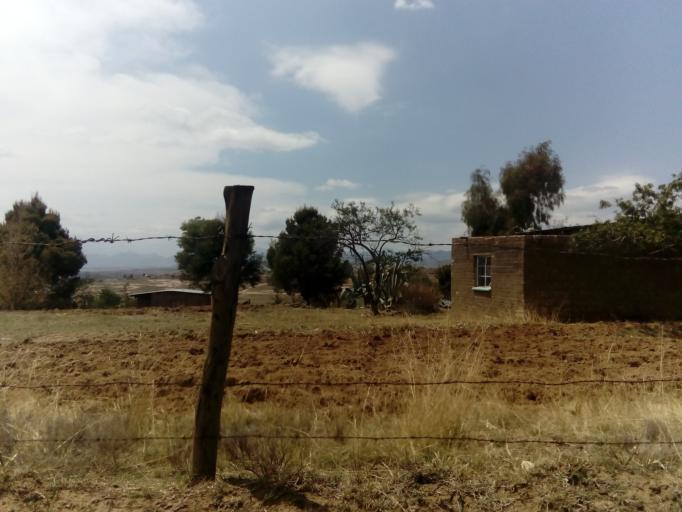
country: LS
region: Berea
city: Teyateyaneng
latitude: -29.2012
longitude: 27.7680
